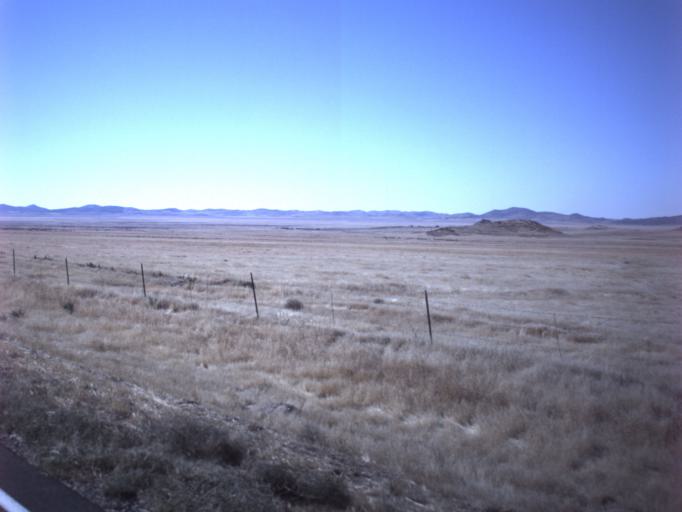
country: US
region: Utah
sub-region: Tooele County
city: Grantsville
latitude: 40.3948
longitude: -112.7476
